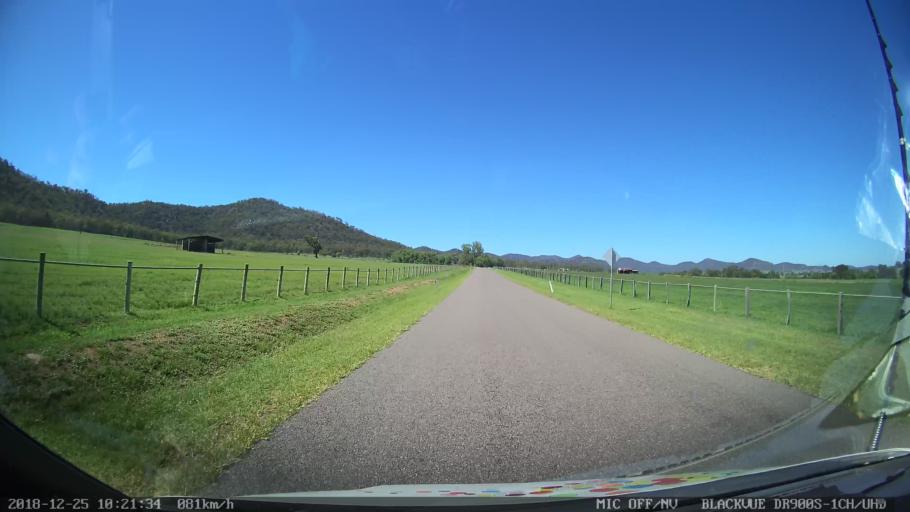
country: AU
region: New South Wales
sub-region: Muswellbrook
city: Denman
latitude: -32.3688
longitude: 150.5409
